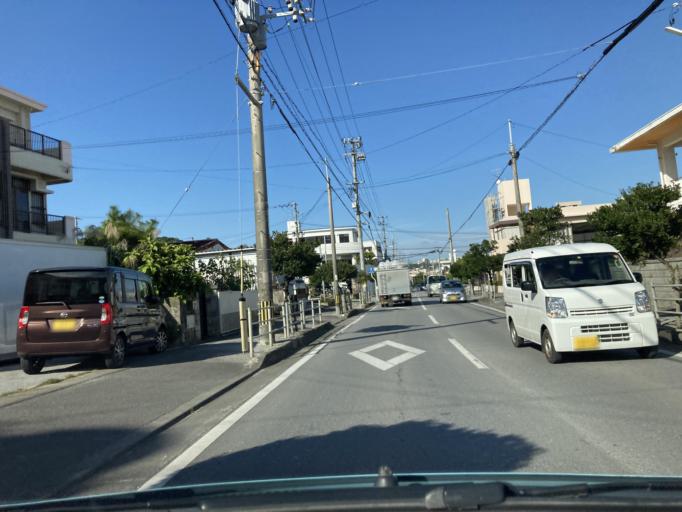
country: JP
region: Okinawa
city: Tomigusuku
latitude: 26.1811
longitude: 127.7068
